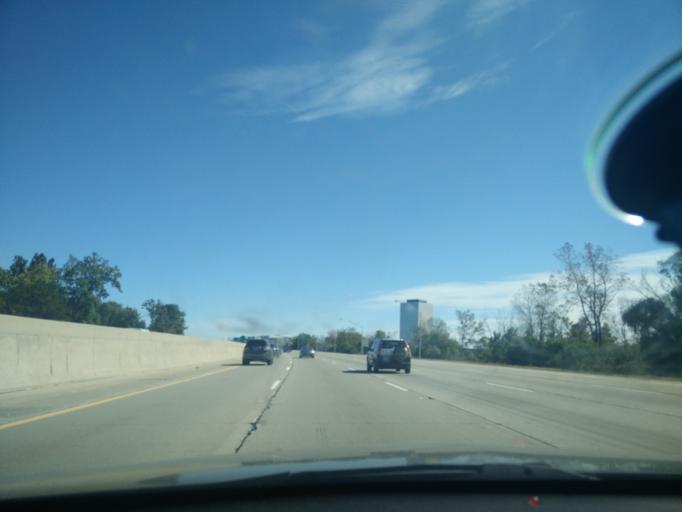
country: US
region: Michigan
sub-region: Oakland County
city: Franklin
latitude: 42.4908
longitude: -83.3117
